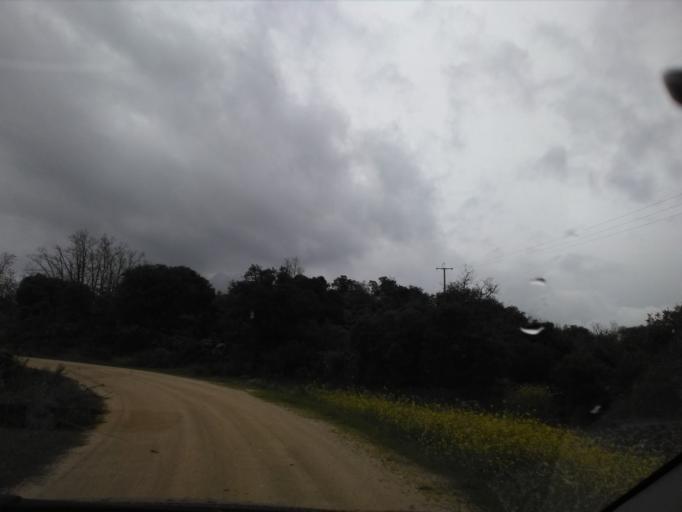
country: ES
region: Castille and Leon
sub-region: Provincia de Salamanca
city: Puerto Seguro
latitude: 40.8354
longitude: -6.7368
